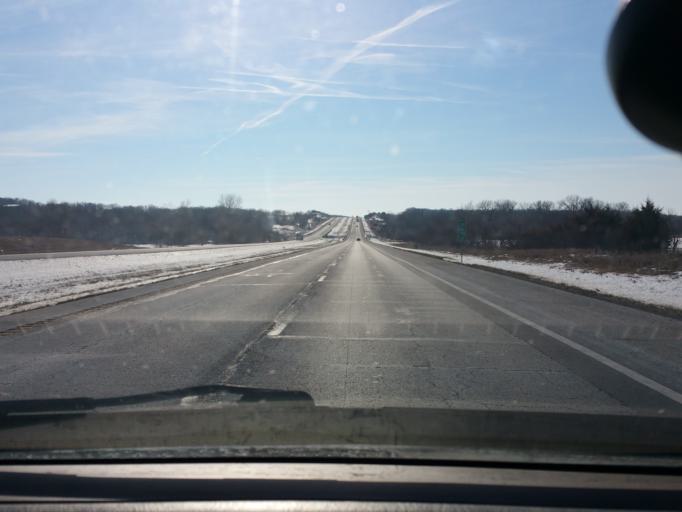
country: US
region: Missouri
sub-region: Harrison County
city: Bethany
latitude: 40.2365
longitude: -94.0131
